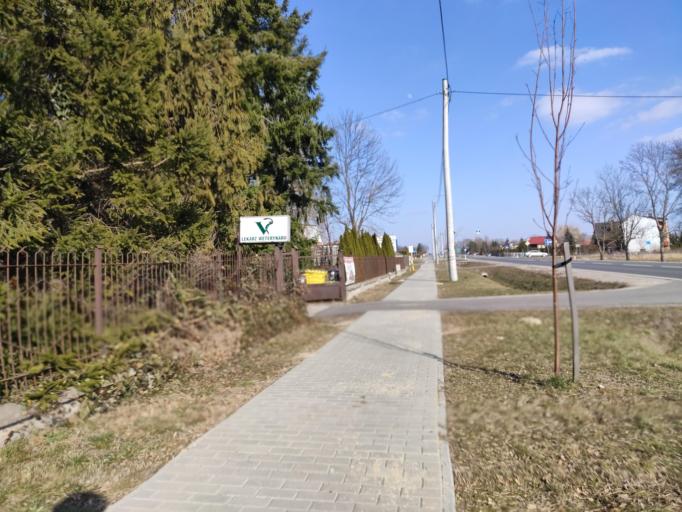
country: PL
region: Lublin Voivodeship
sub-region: Powiat lubartowski
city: Kock
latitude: 51.6423
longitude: 22.4284
